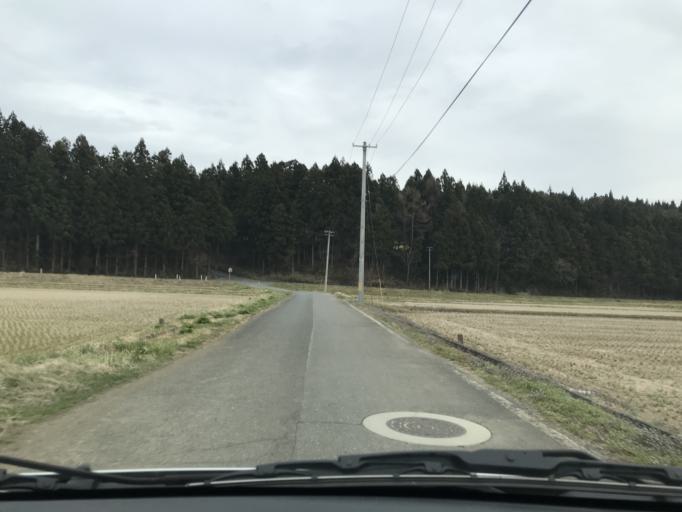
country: JP
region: Iwate
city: Mizusawa
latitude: 39.0506
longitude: 141.1652
